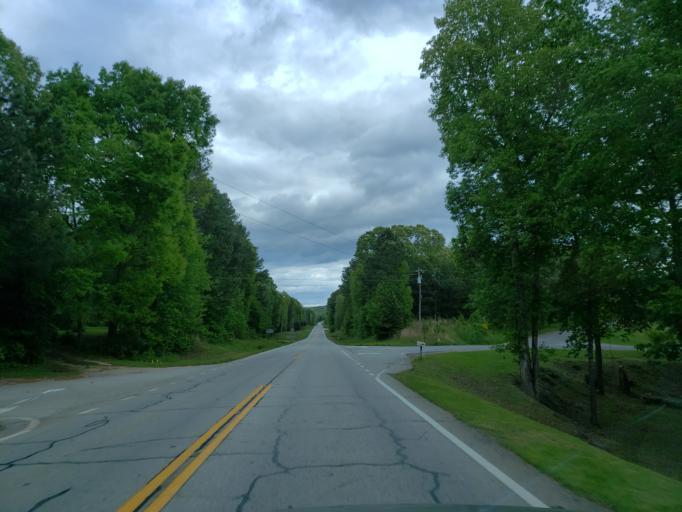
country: US
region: Georgia
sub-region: Carroll County
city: Temple
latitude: 33.8223
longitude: -85.0800
